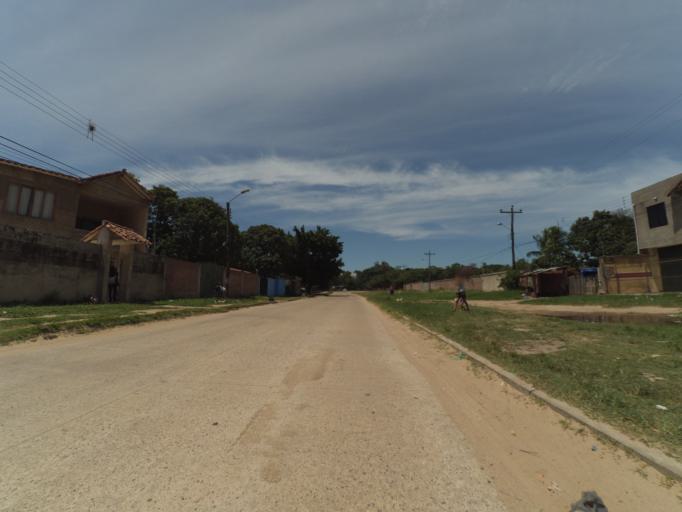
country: BO
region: Santa Cruz
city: Santa Cruz de la Sierra
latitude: -17.8073
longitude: -63.2232
